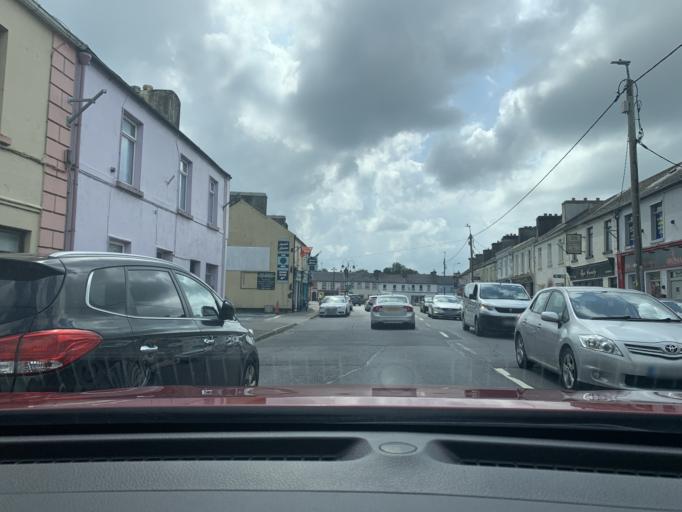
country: IE
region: Connaught
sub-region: Sligo
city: Tobercurry
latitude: 53.9649
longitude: -8.7954
